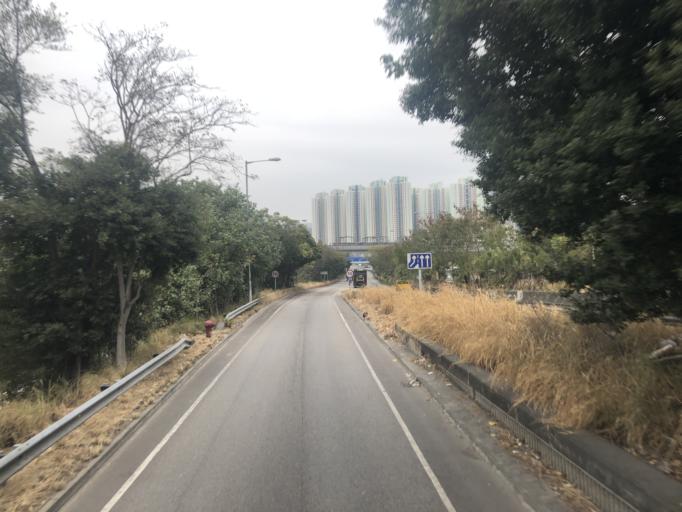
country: HK
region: Yuen Long
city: Yuen Long Kau Hui
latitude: 22.4406
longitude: 113.9985
